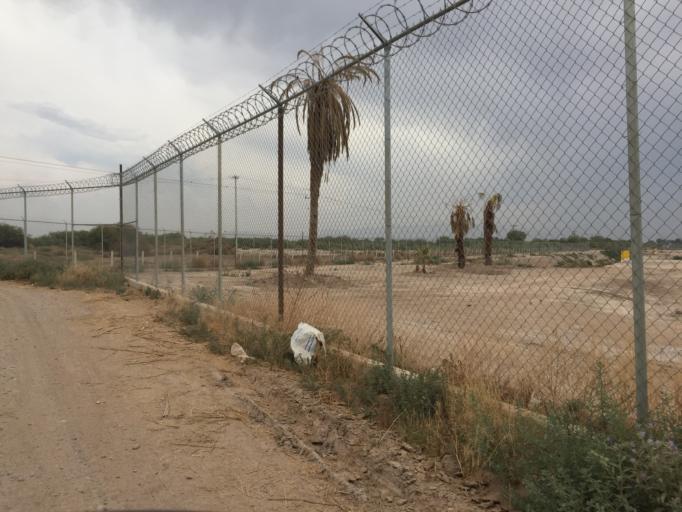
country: MX
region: Durango
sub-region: Gomez Palacio
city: San Jose de Vinedo
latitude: 25.6558
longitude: -103.4424
